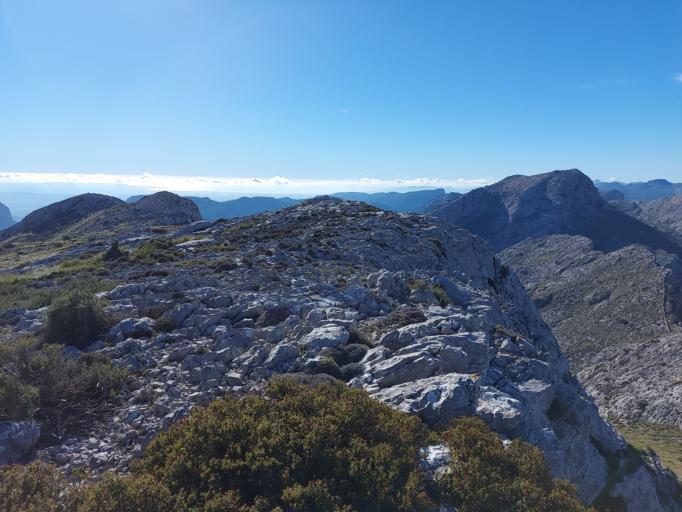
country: ES
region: Balearic Islands
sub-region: Illes Balears
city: Fornalutx
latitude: 39.7871
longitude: 2.8084
